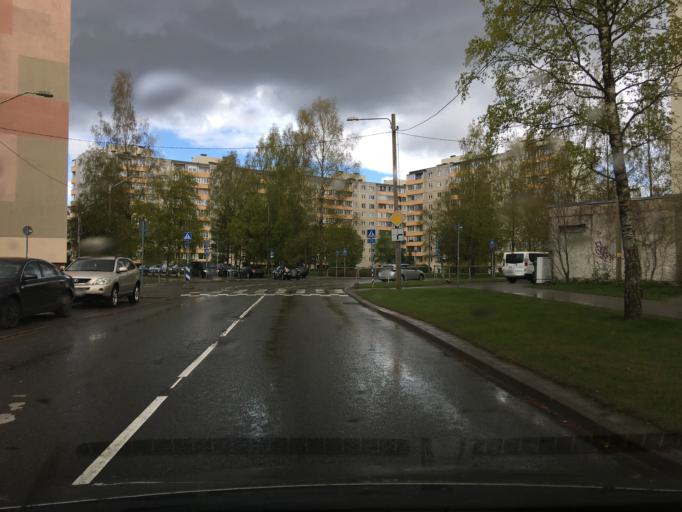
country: EE
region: Harju
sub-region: Tallinna linn
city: Kose
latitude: 59.4408
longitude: 24.8778
